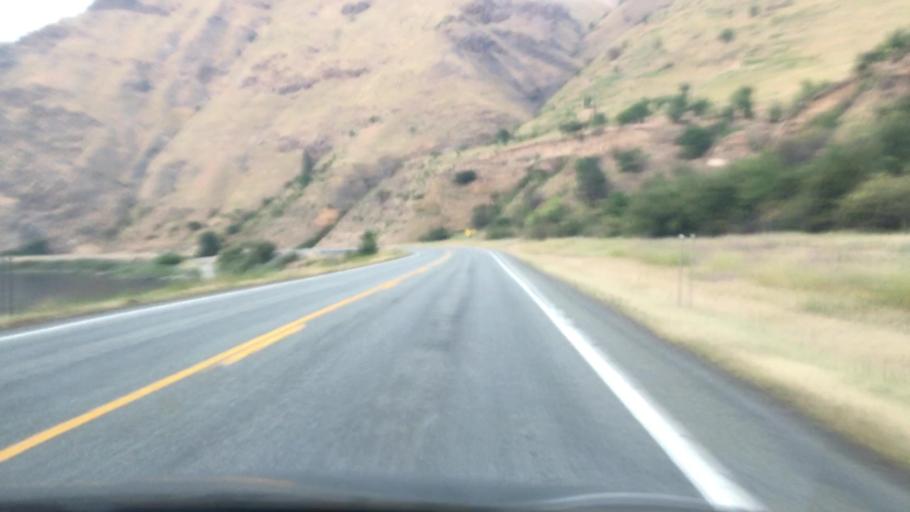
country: US
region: Idaho
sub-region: Idaho County
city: Grangeville
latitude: 45.5957
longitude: -116.2772
